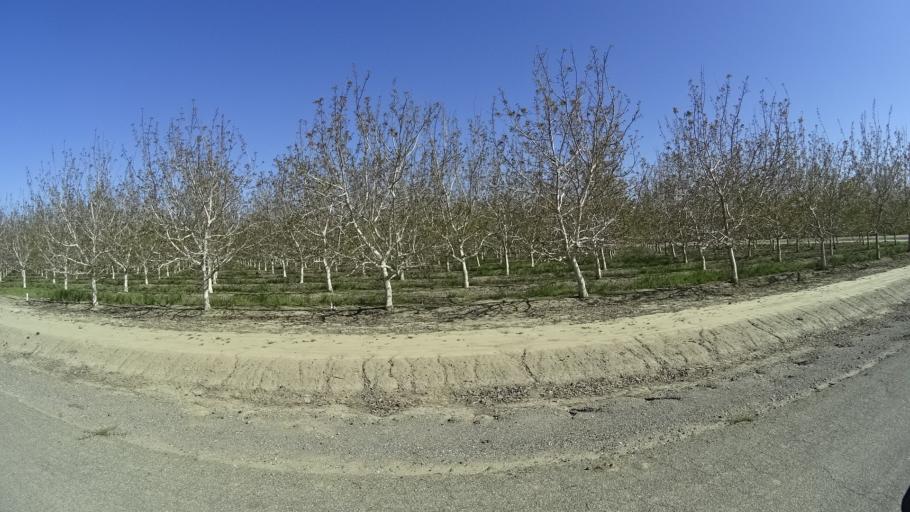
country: US
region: California
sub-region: Glenn County
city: Hamilton City
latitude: 39.7129
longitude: -121.9852
